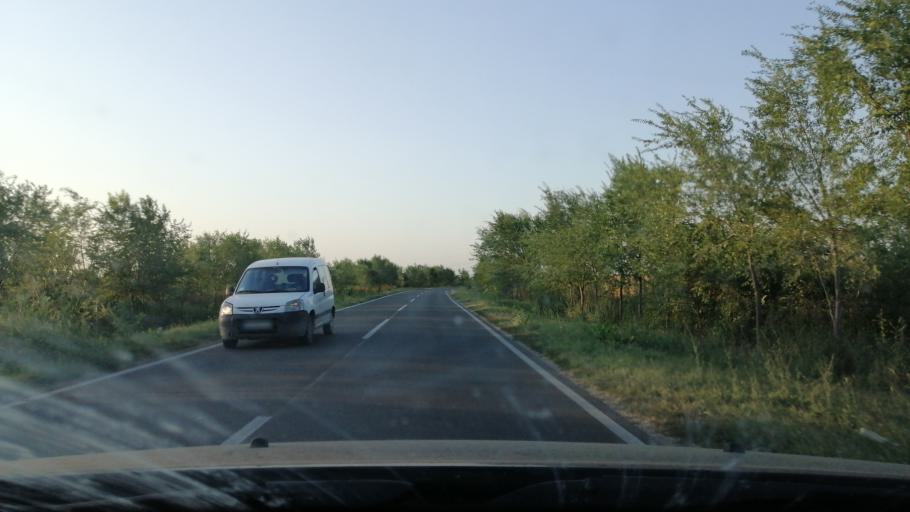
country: RS
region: Central Serbia
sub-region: Belgrade
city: Grocka
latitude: 44.7798
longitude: 20.7238
